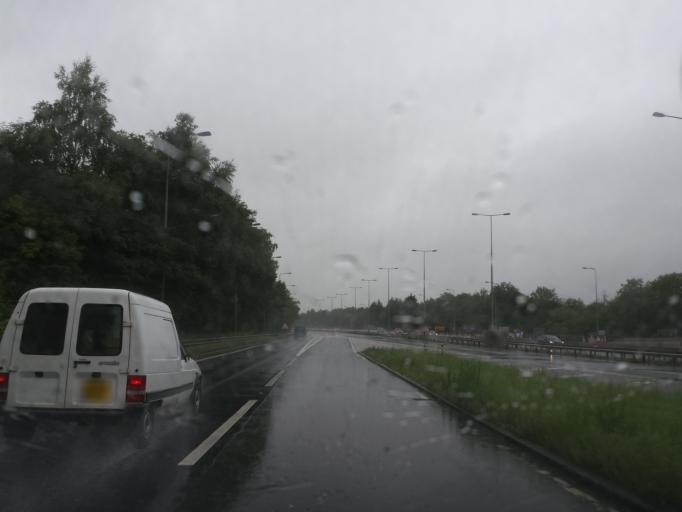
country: GB
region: England
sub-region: Coventry
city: Coventry
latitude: 52.3759
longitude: -1.5032
